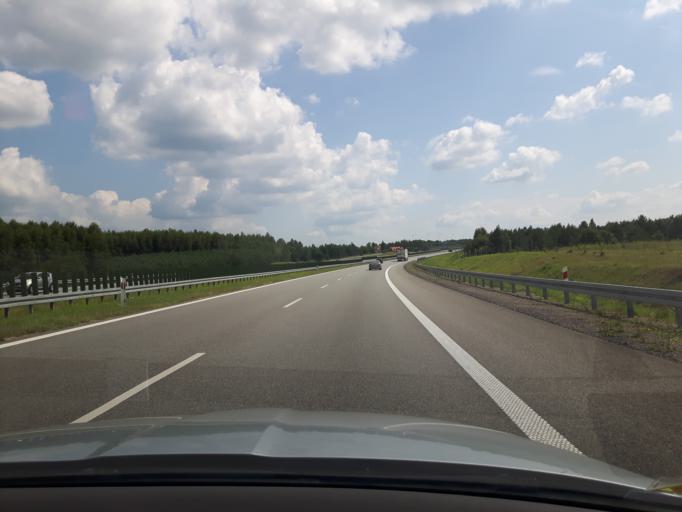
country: PL
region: Warmian-Masurian Voivodeship
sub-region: Powiat ostrodzki
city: Milomlyn
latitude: 53.7728
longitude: 19.8416
